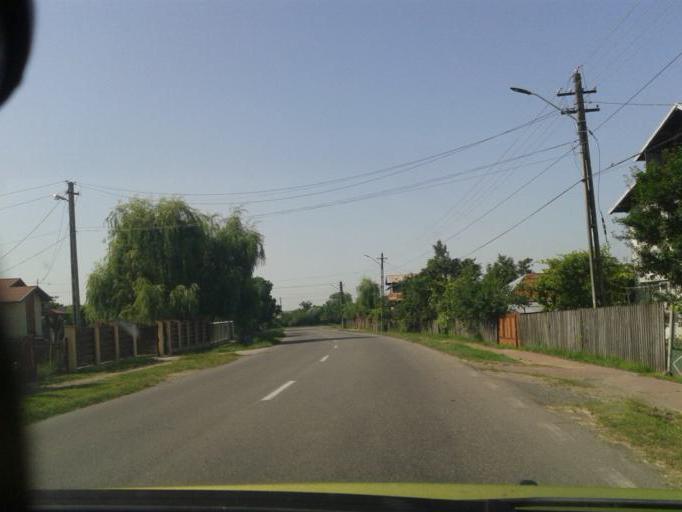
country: RO
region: Prahova
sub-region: Comuna Dumbravesti
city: Dumbravesti
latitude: 45.0842
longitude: 25.9955
